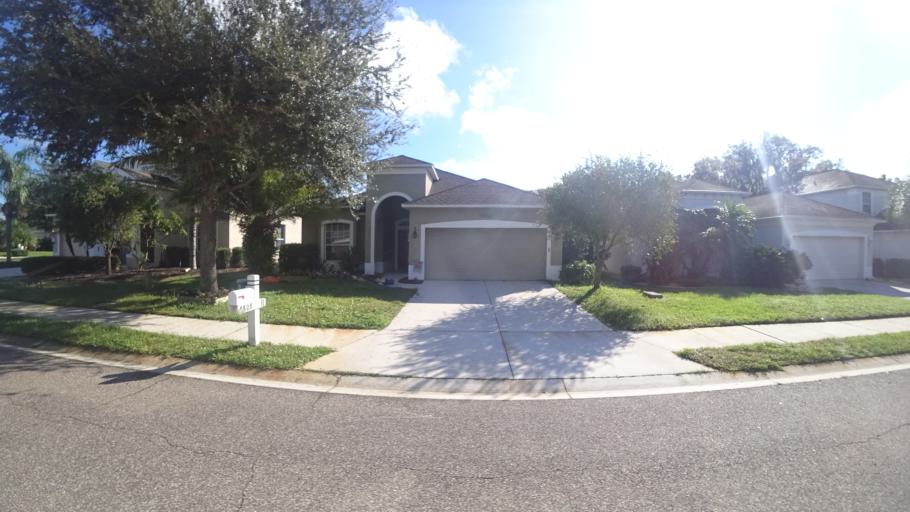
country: US
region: Florida
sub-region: Manatee County
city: Ellenton
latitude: 27.5903
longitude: -82.5004
